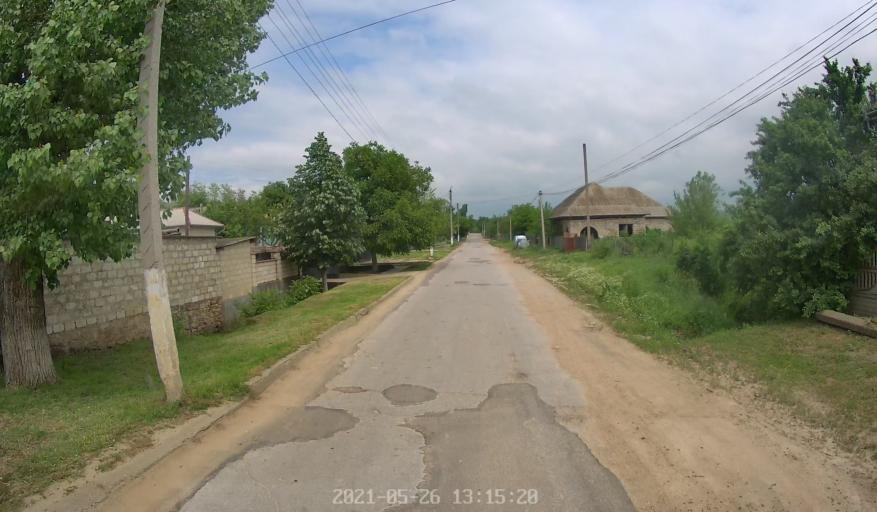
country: MD
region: Hincesti
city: Dancu
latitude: 46.7596
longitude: 28.3410
